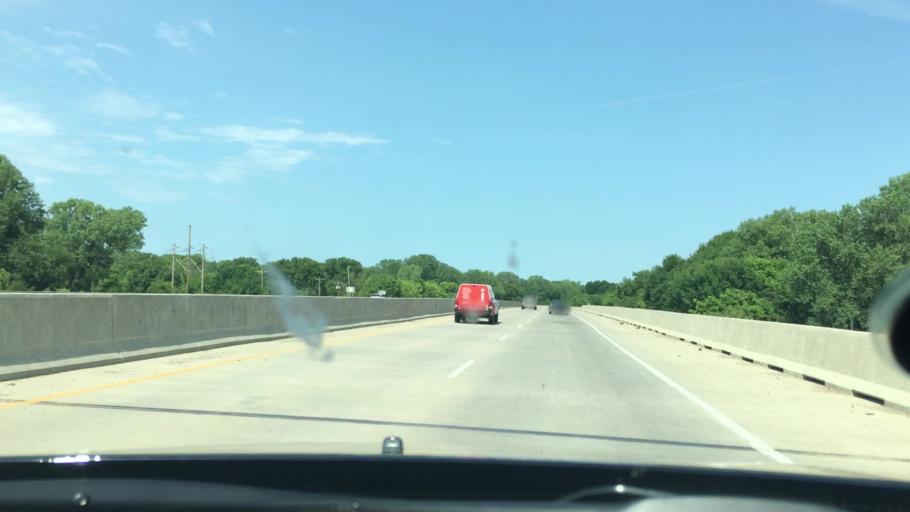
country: US
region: Oklahoma
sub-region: Murray County
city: Davis
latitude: 34.5049
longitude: -97.1408
